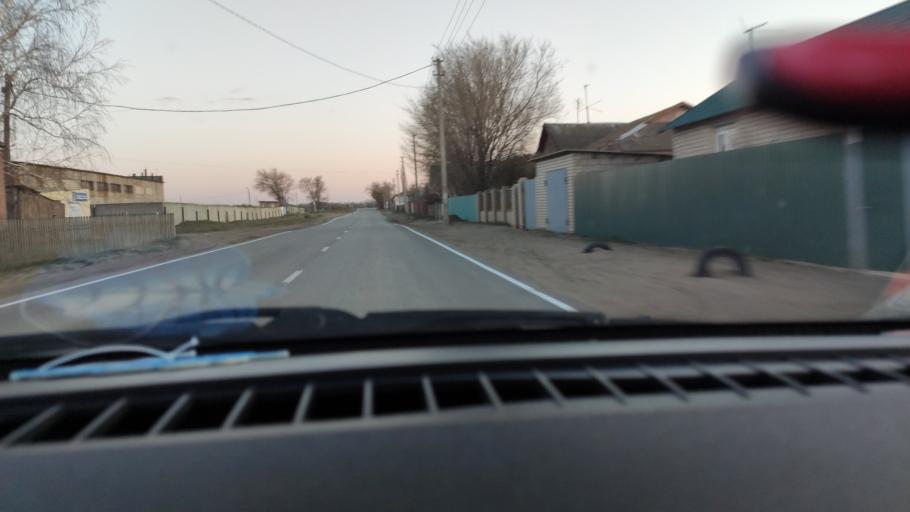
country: RU
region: Saratov
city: Privolzhskiy
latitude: 51.1970
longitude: 45.9154
